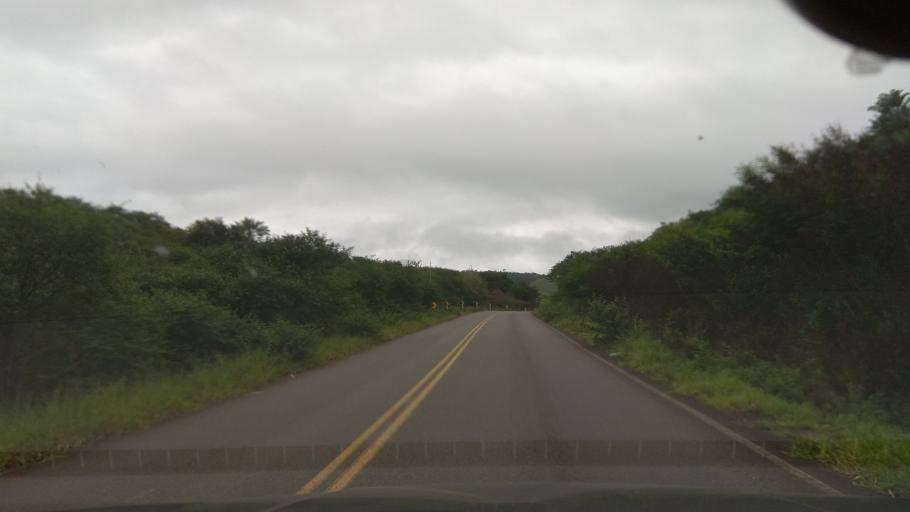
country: BR
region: Bahia
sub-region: Santa Ines
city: Santa Ines
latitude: -13.2565
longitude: -39.7835
